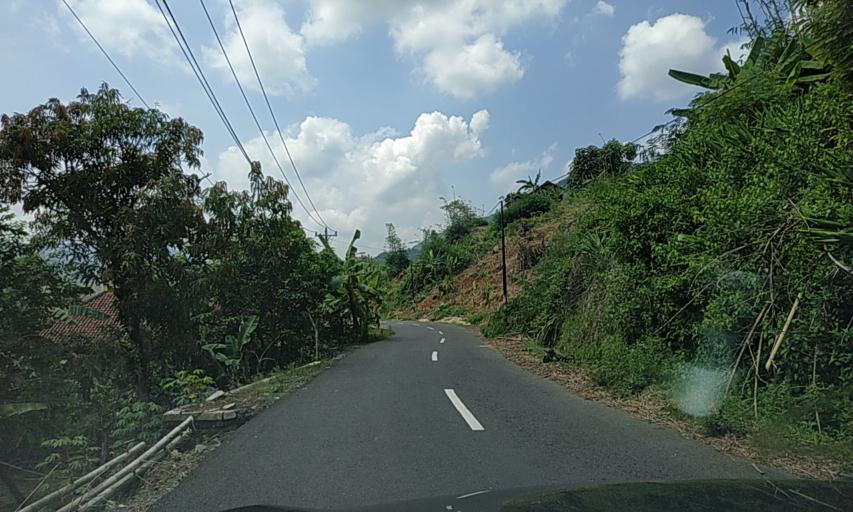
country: ID
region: Central Java
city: Kutoarjo
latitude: -7.6242
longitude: 109.7281
